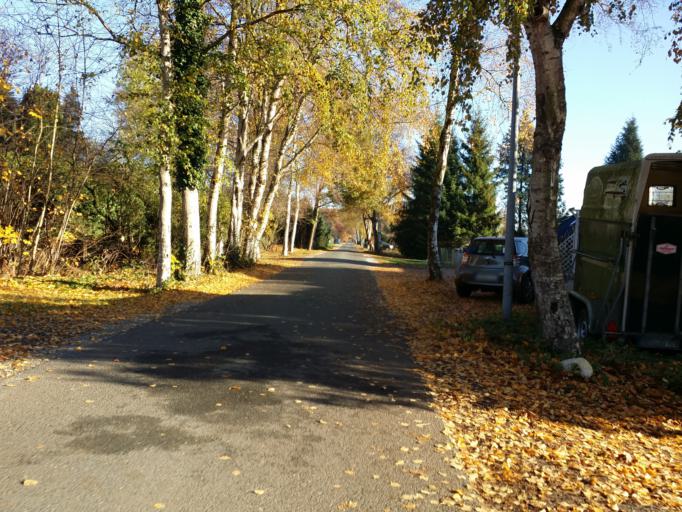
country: DE
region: Lower Saxony
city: Oyten
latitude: 53.0716
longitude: 8.9750
